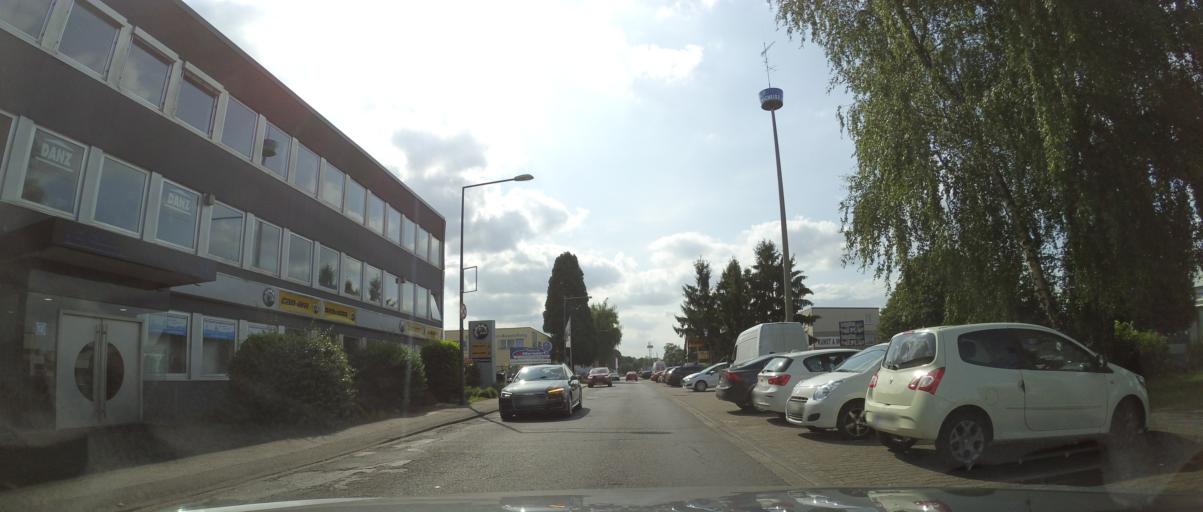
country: DE
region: North Rhine-Westphalia
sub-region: Regierungsbezirk Koln
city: Frechen
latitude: 50.9210
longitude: 6.8516
